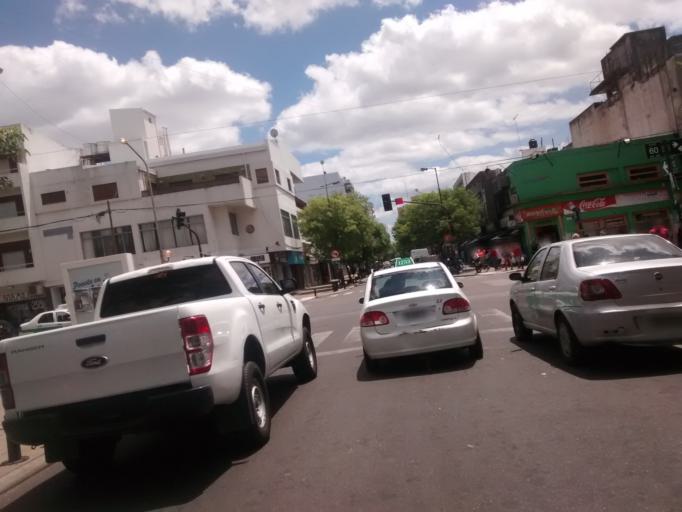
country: AR
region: Buenos Aires
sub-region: Partido de La Plata
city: La Plata
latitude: -34.9257
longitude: -57.9464
